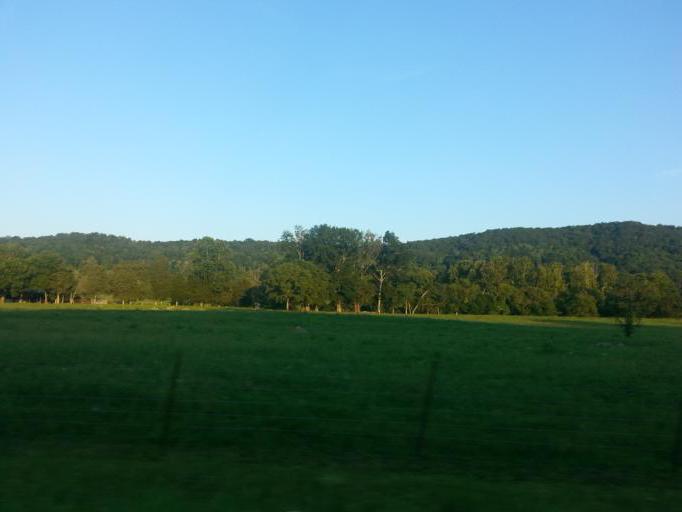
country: US
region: Tennessee
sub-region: Roane County
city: Midtown
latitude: 35.7753
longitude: -84.5836
